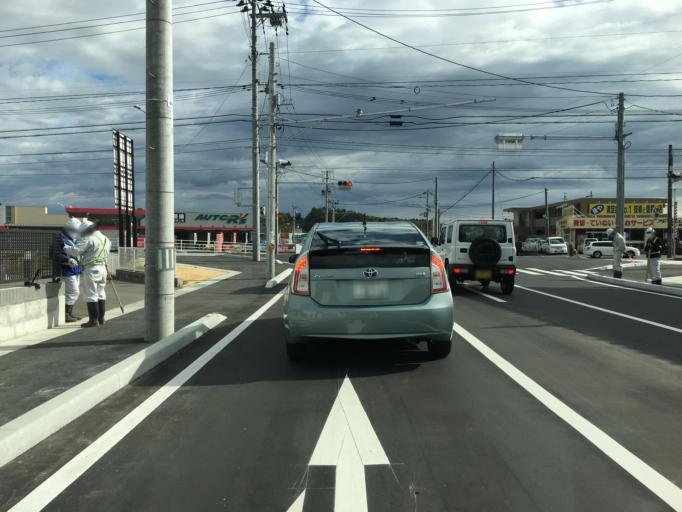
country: JP
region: Fukushima
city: Nihommatsu
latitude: 37.6118
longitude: 140.4610
